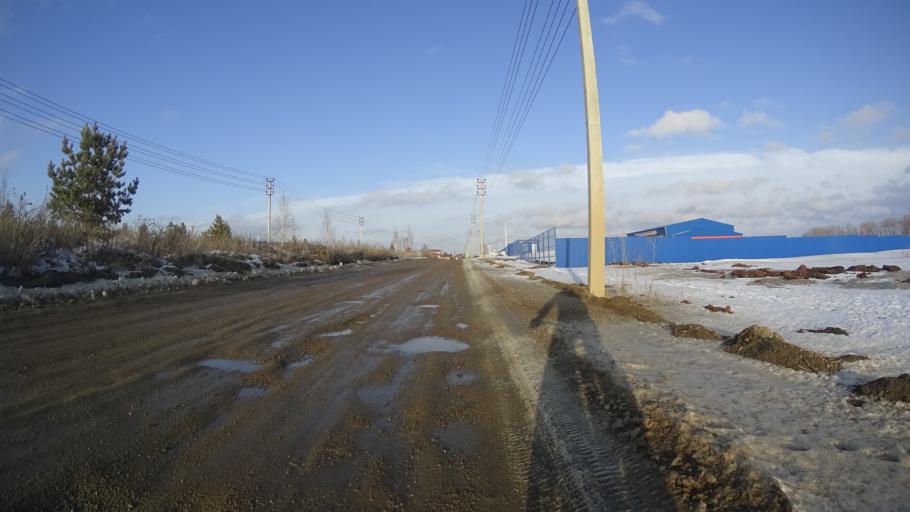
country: RU
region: Chelyabinsk
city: Sargazy
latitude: 55.1070
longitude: 61.2693
